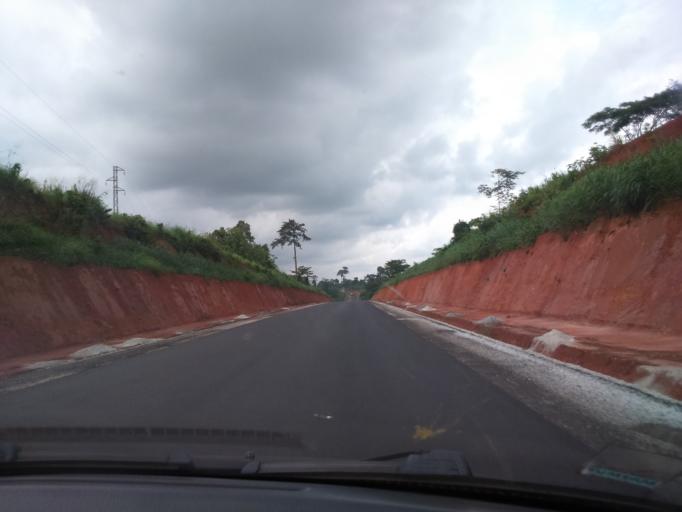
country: CI
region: Lagunes
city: Akoupe
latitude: 6.5041
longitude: -3.8222
